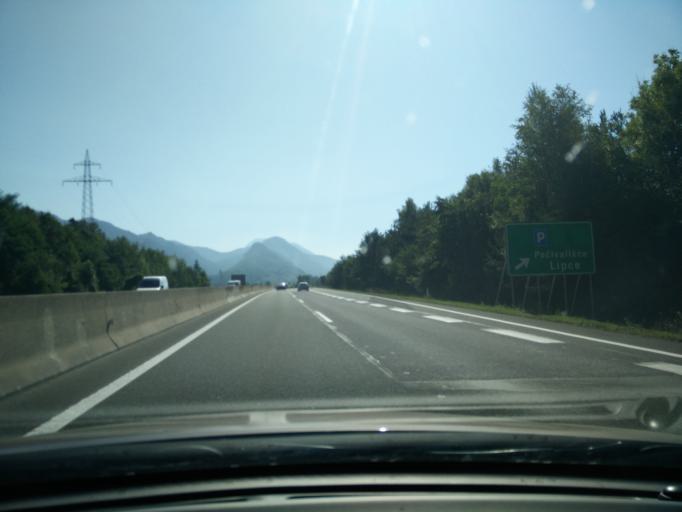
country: SI
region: Bled
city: Zasip
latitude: 46.4128
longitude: 14.1064
